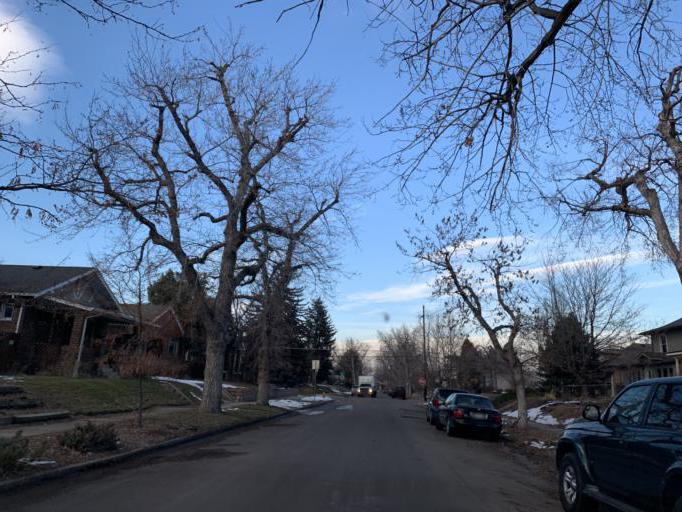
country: US
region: Colorado
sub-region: Jefferson County
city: Edgewater
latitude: 39.7777
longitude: -105.0451
